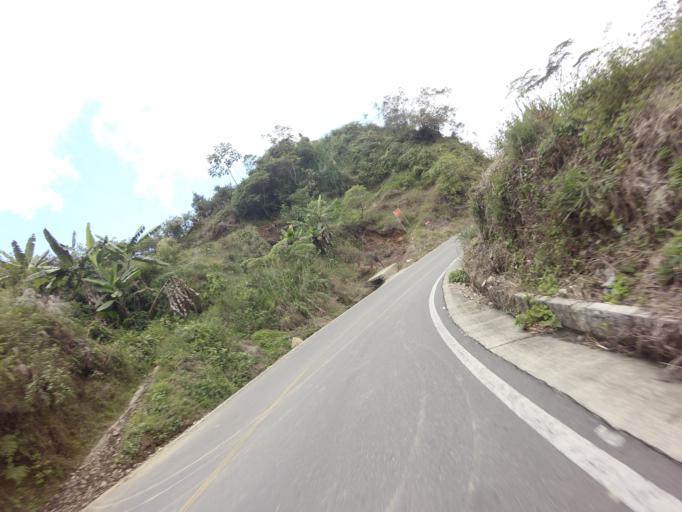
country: CO
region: Caldas
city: Marquetalia
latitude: 5.2751
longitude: -75.1029
